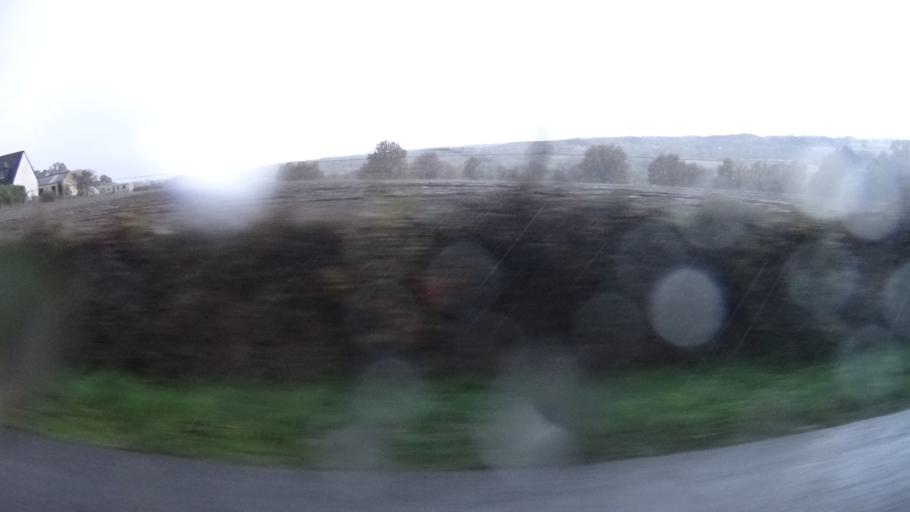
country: FR
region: Pays de la Loire
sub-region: Departement de la Loire-Atlantique
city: Avessac
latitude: 47.6756
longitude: -1.9833
